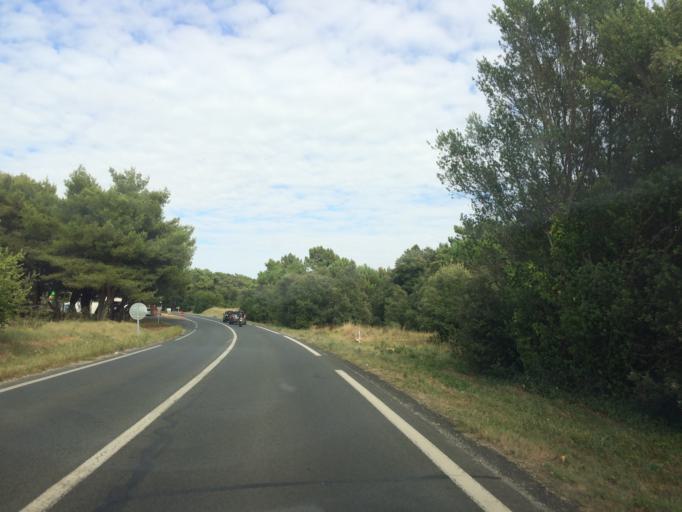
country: FR
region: Poitou-Charentes
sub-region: Departement de la Charente-Maritime
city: La Flotte
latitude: 46.1786
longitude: -1.3293
